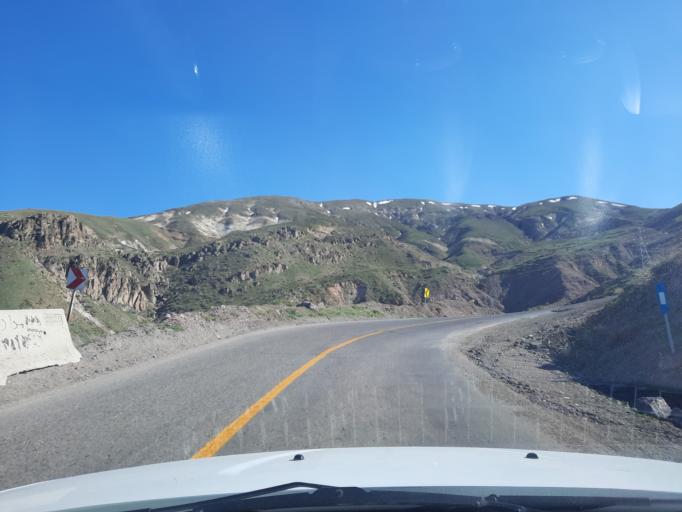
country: IR
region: Qazvin
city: Qazvin
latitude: 36.4042
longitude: 50.2255
